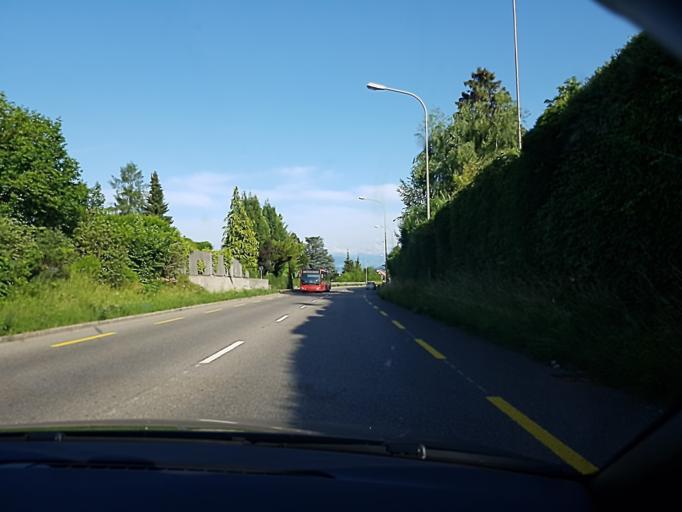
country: CH
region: Zurich
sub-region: Bezirk Horgen
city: Thalwil / Nord
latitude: 47.2986
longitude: 8.5526
